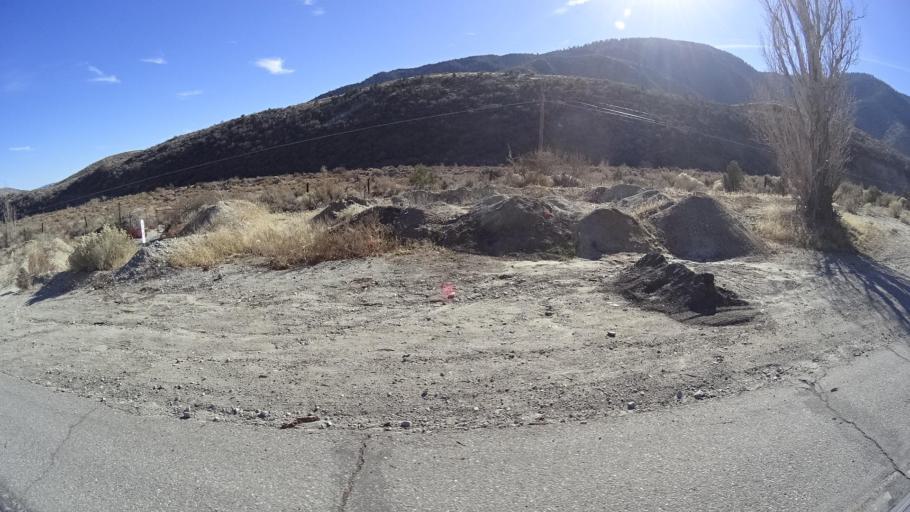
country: US
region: California
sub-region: Kern County
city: Frazier Park
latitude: 34.8213
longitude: -118.9273
